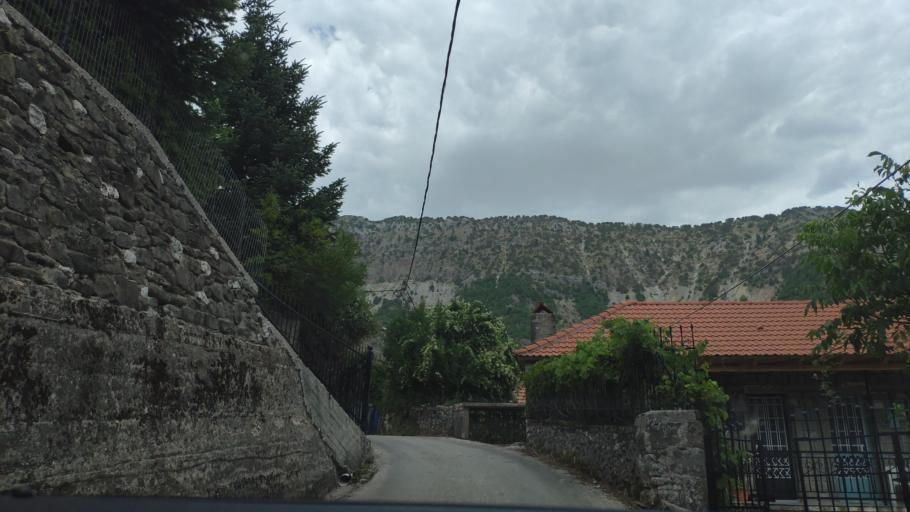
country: GR
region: Epirus
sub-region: Nomos Artas
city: Voulgareli
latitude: 39.4353
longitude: 21.2102
